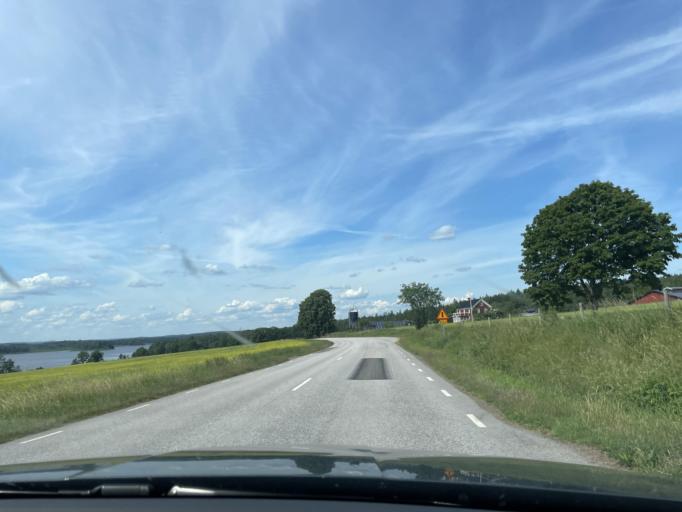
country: SE
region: Kalmar
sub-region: Vimmerby Kommun
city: Vimmerby
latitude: 57.7137
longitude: 15.8366
